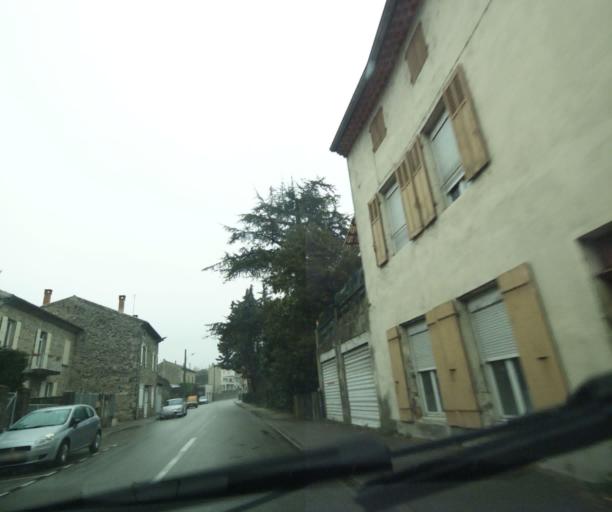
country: FR
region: Rhone-Alpes
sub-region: Departement de l'Ardeche
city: Saint-Privat
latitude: 44.6260
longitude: 4.4069
